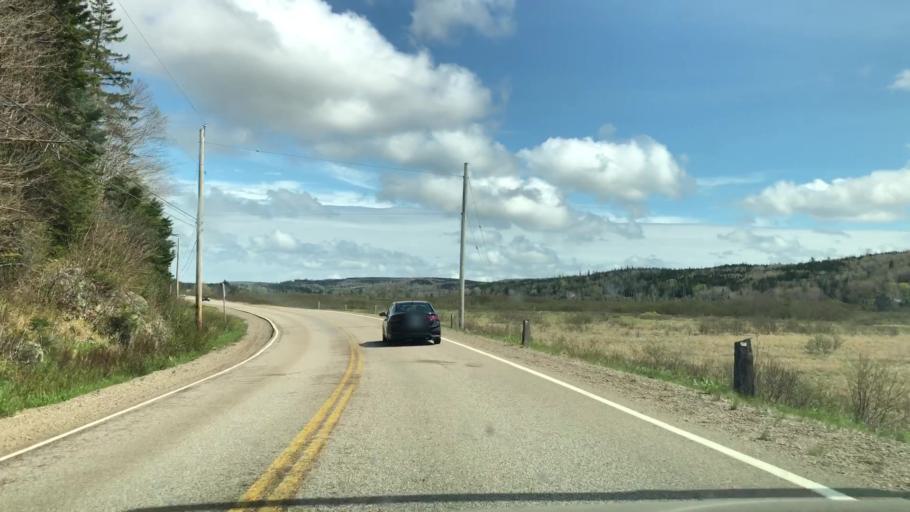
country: CA
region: Nova Scotia
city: Antigonish
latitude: 45.1961
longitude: -62.0010
